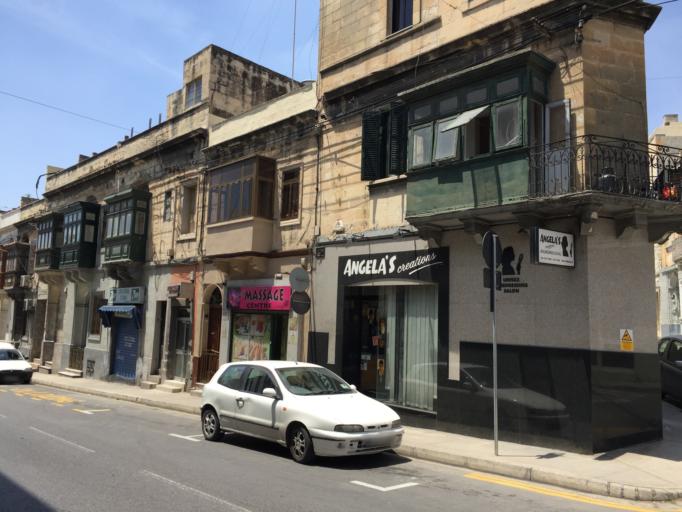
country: MT
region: Ta' Xbiex
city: Ta' Xbiex
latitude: 35.8974
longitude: 14.4897
